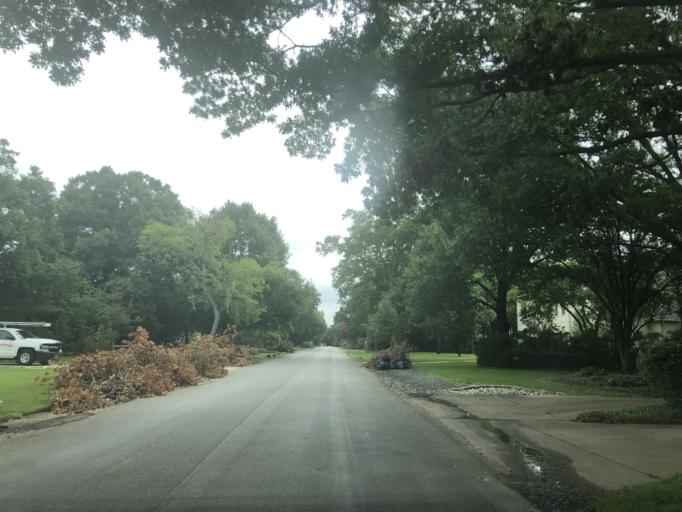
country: US
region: Texas
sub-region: Dallas County
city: University Park
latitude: 32.8546
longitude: -96.8354
